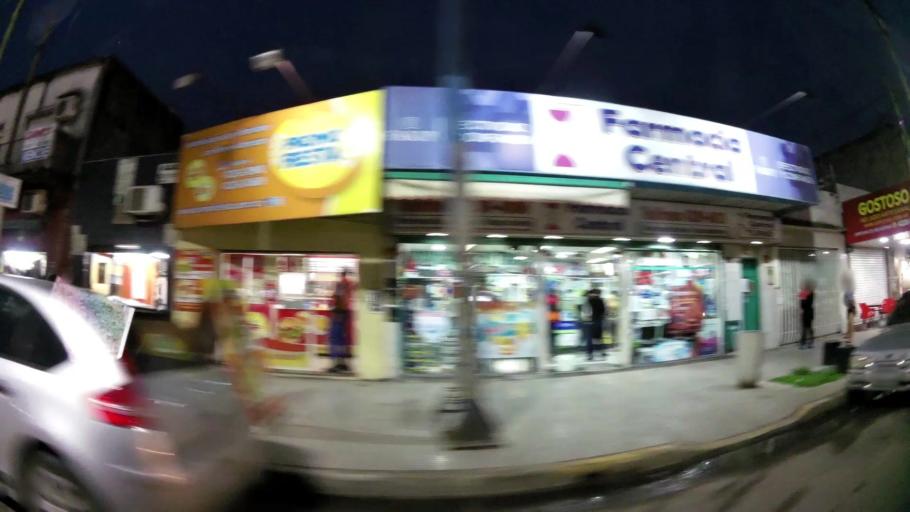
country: AR
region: Buenos Aires
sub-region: Partido de Lanus
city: Lanus
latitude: -34.7296
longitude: -58.3522
